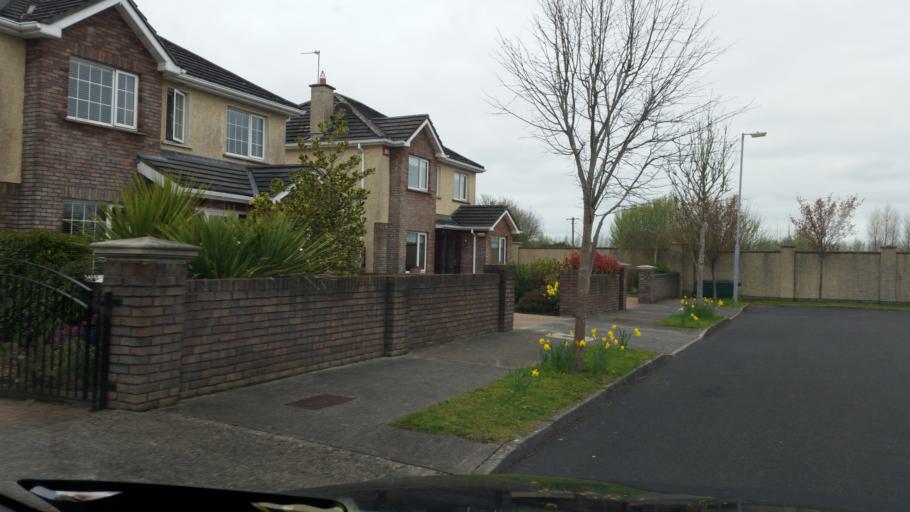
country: IE
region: Leinster
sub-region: An Iarmhi
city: An Muileann gCearr
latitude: 53.5228
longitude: -7.3052
